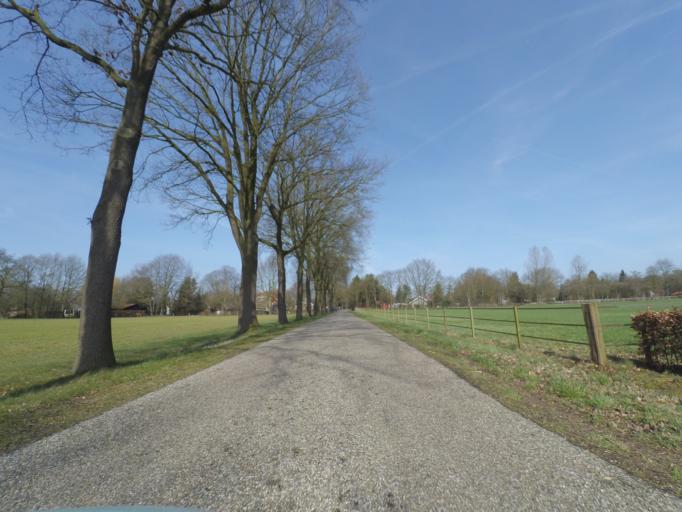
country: NL
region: Gelderland
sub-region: Gemeente Barneveld
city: Voorthuizen
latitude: 52.2115
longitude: 5.6287
